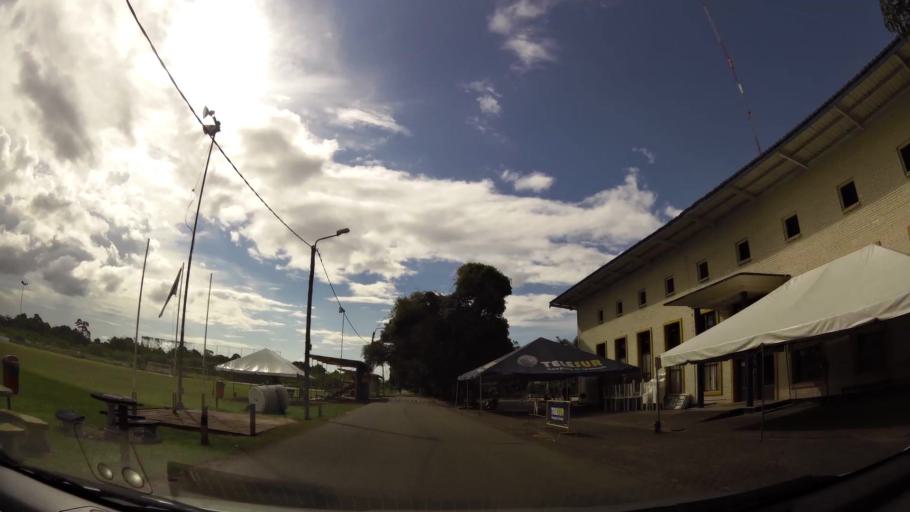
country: SR
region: Paramaribo
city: Paramaribo
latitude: 5.8496
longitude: -55.1584
